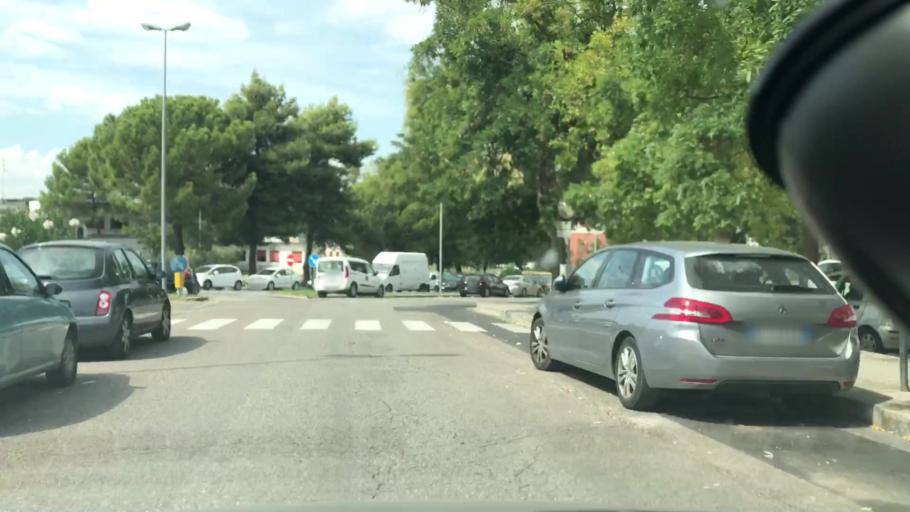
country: IT
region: Basilicate
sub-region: Provincia di Matera
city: Matera
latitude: 40.6750
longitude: 16.5843
